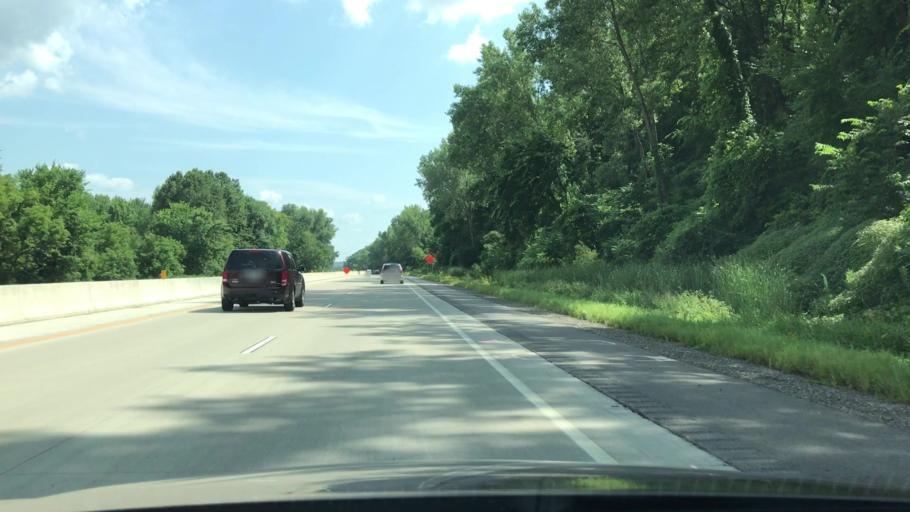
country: US
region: Minnesota
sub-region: Nicollet County
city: North Mankato
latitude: 44.2124
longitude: -94.0268
